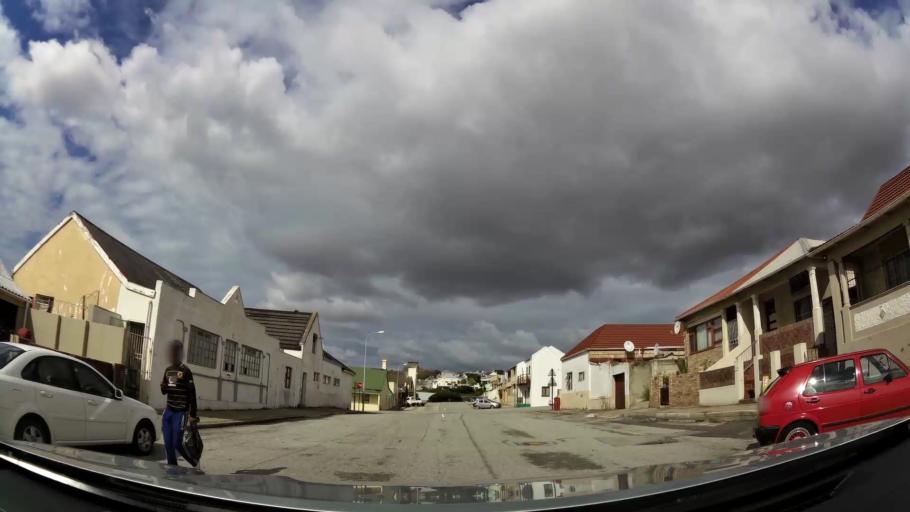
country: ZA
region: Eastern Cape
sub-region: Nelson Mandela Bay Metropolitan Municipality
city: Port Elizabeth
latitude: -33.9535
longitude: 25.6083
